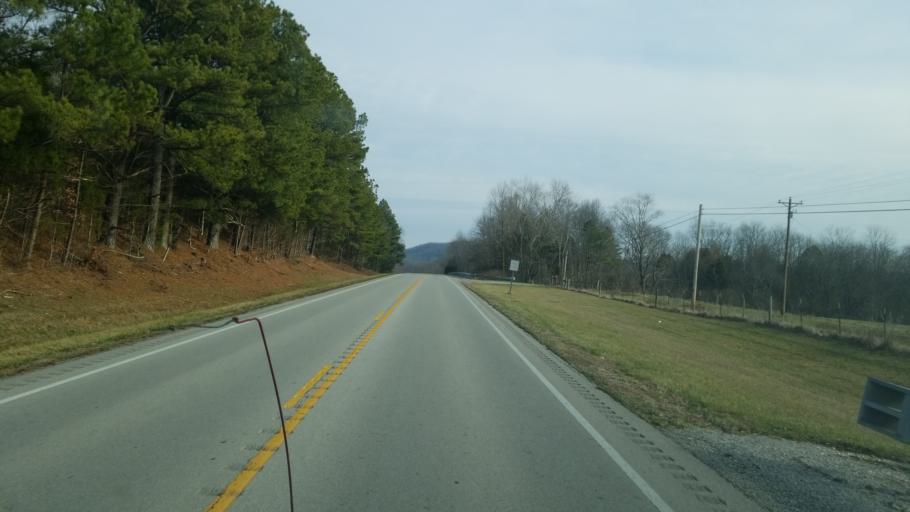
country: US
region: Kentucky
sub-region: Casey County
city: Liberty
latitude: 37.3520
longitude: -84.8721
